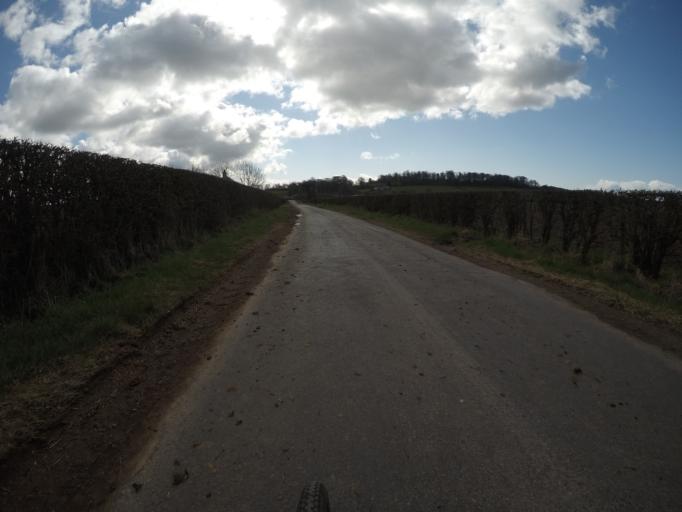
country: GB
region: Scotland
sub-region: South Ayrshire
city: Dundonald
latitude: 55.5882
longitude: -4.5773
